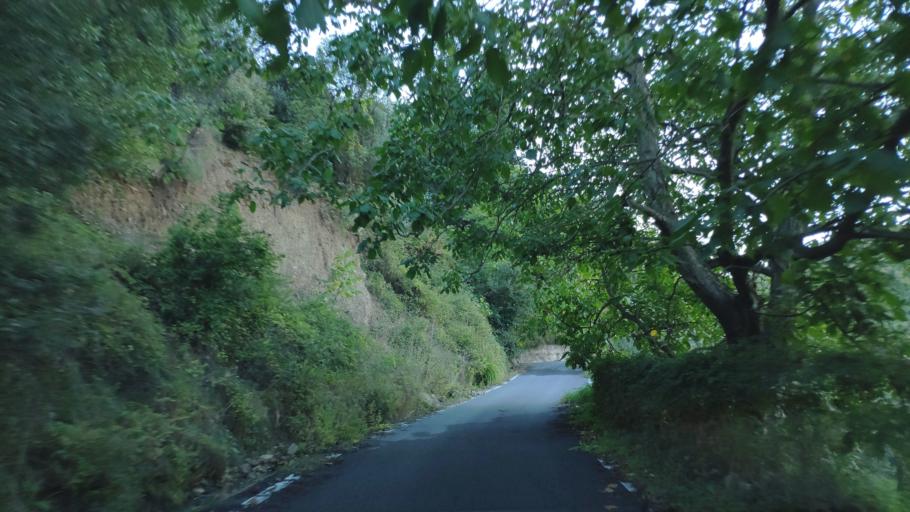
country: GR
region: Peloponnese
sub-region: Nomos Arkadias
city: Dimitsana
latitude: 37.5706
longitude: 22.0447
